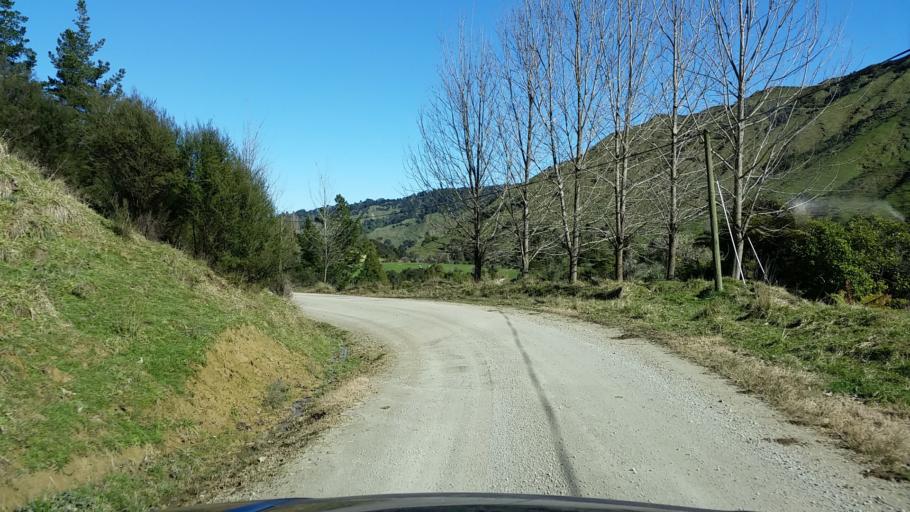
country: NZ
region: Manawatu-Wanganui
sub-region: Wanganui District
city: Wanganui
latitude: -39.5356
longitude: 174.9247
